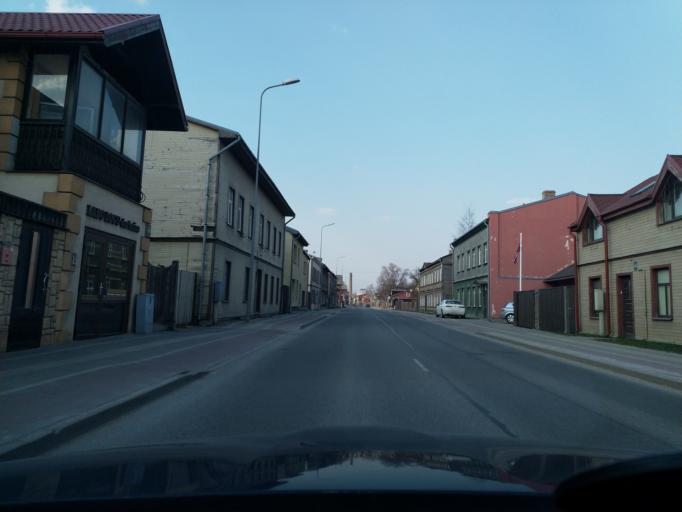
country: LV
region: Liepaja
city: Liepaja
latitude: 56.5037
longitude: 21.0236
